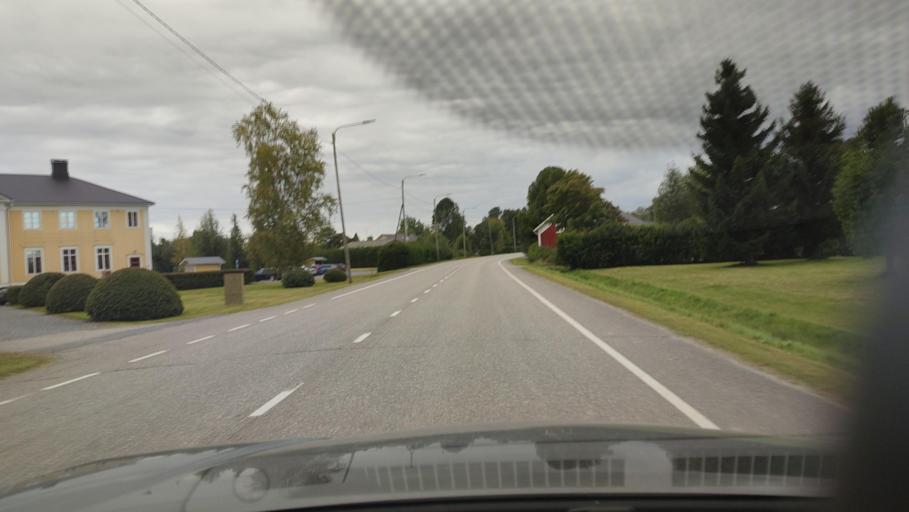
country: FI
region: Ostrobothnia
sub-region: Sydosterbotten
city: Kristinestad
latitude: 62.2562
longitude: 21.5160
